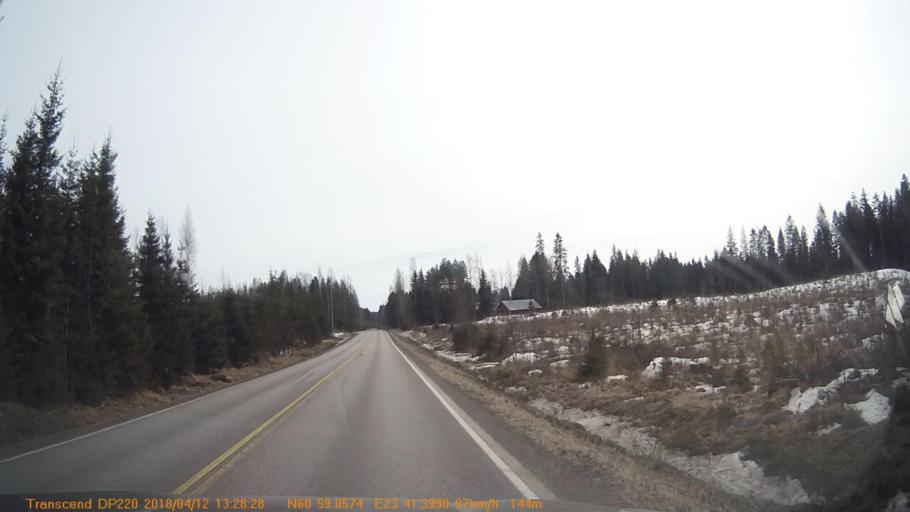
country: FI
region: Pirkanmaa
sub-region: Etelae-Pirkanmaa
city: Kylmaekoski
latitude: 60.9840
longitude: 23.6902
